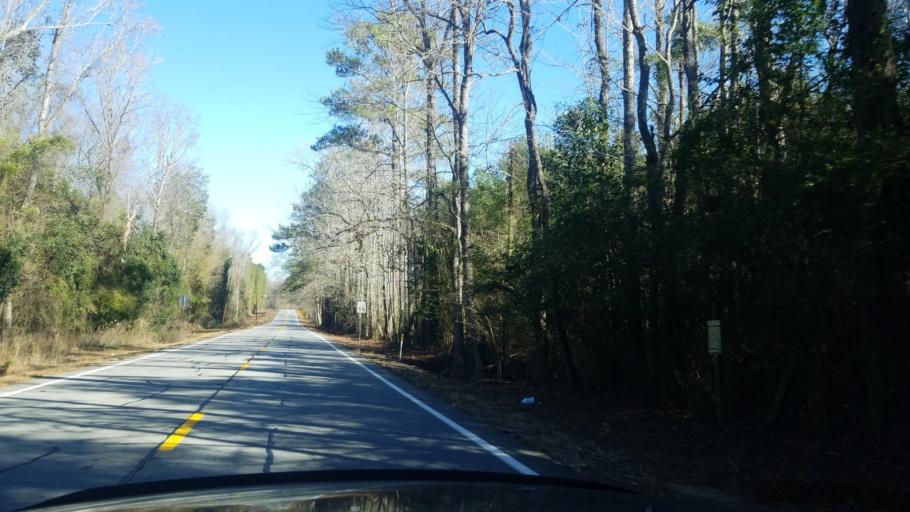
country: US
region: Georgia
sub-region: Harris County
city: Hamilton
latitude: 32.6588
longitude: -84.8637
